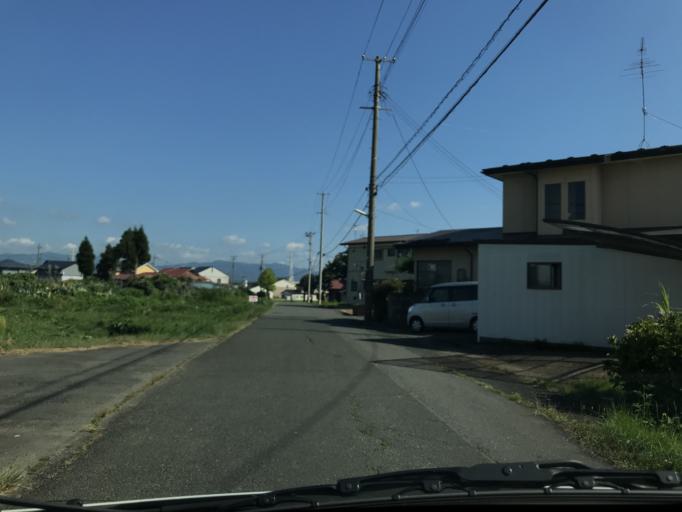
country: JP
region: Iwate
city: Mizusawa
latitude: 39.1568
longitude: 141.1402
